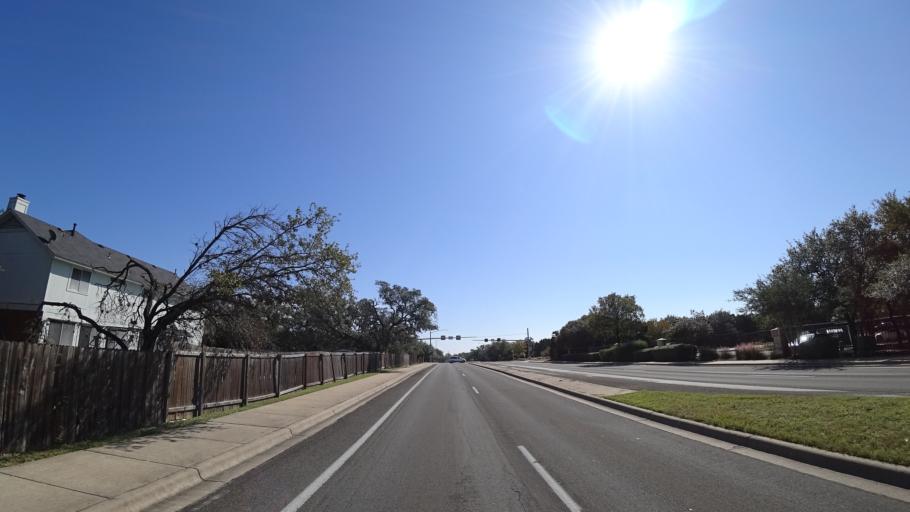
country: US
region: Texas
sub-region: Travis County
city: Shady Hollow
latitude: 30.2048
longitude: -97.8588
